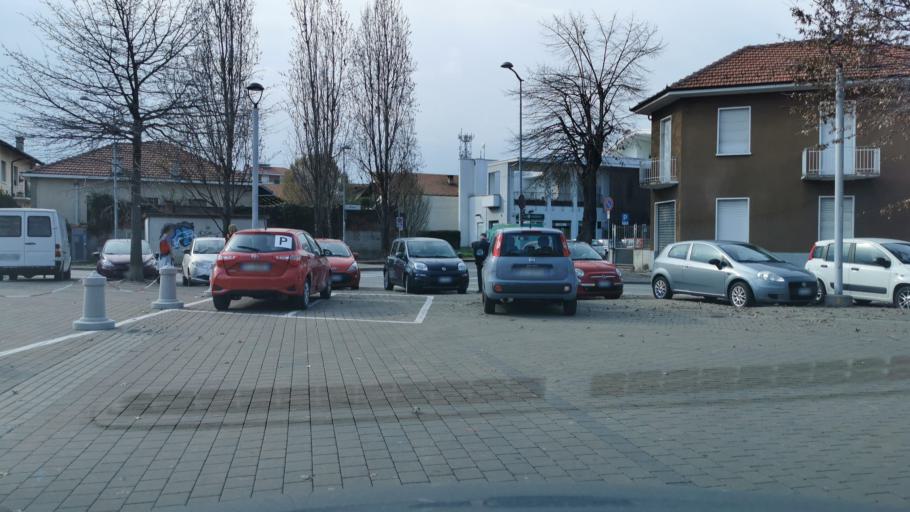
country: IT
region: Piedmont
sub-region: Provincia di Torino
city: Volpiano
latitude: 45.2010
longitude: 7.7820
